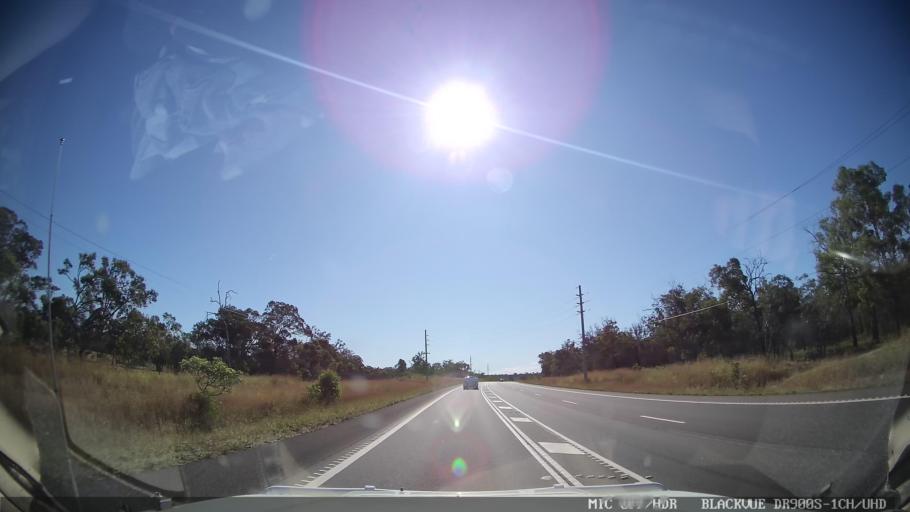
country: AU
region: Queensland
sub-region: Bundaberg
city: Childers
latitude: -25.2728
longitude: 152.3797
